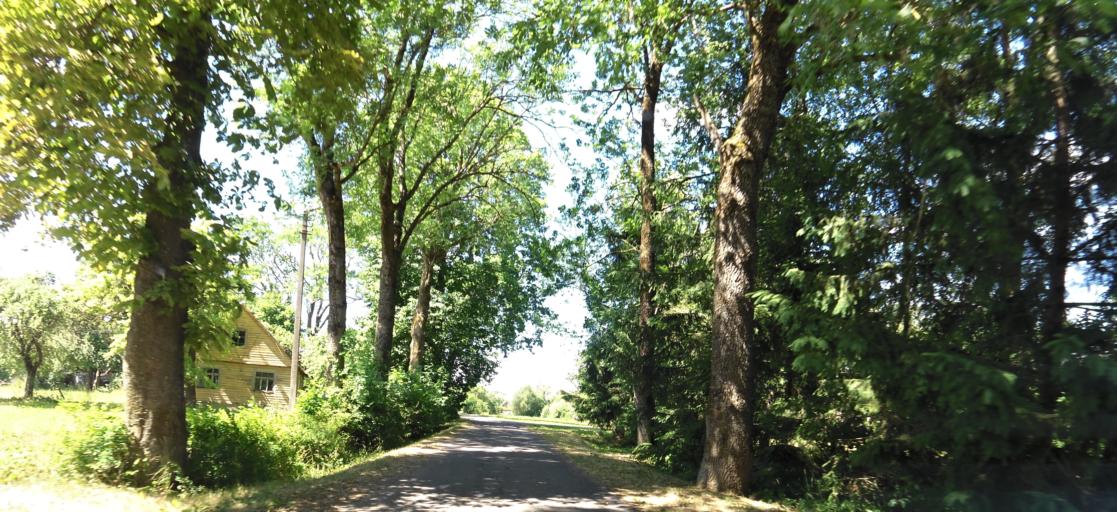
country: LT
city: Kupiskis
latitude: 55.9700
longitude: 25.0006
